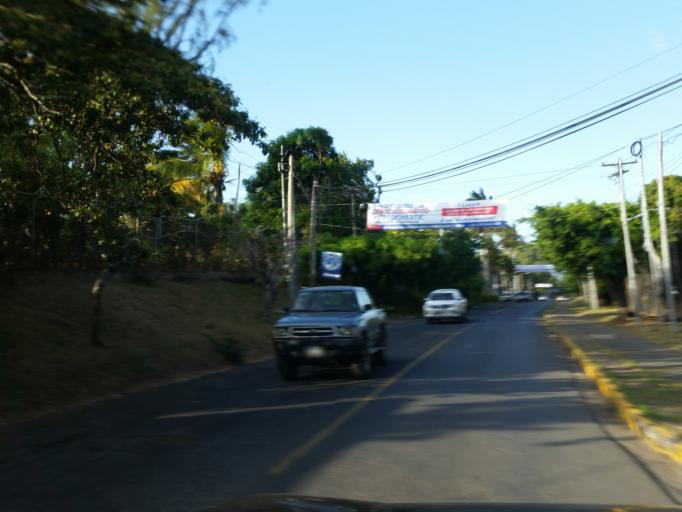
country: NI
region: Managua
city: Managua
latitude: 12.0861
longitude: -86.2405
